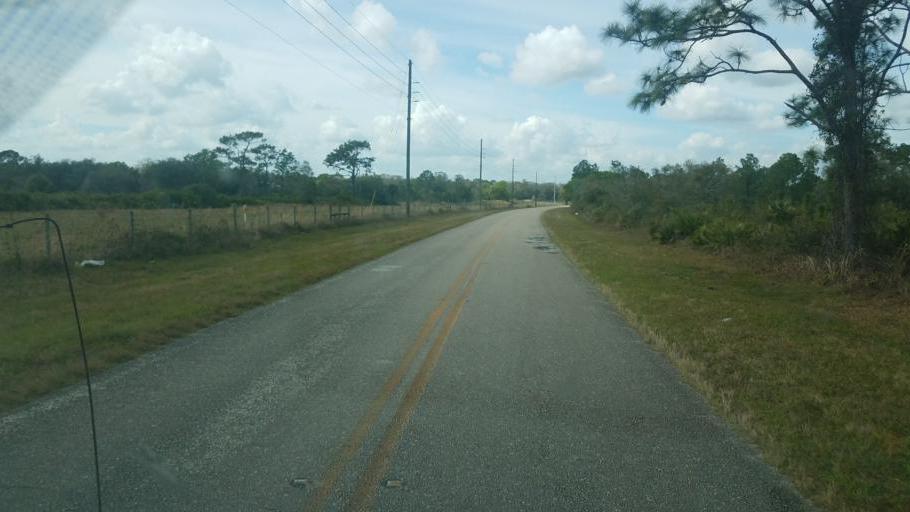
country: US
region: Florida
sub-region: Okeechobee County
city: Cypress Quarters
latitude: 27.5193
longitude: -80.7906
